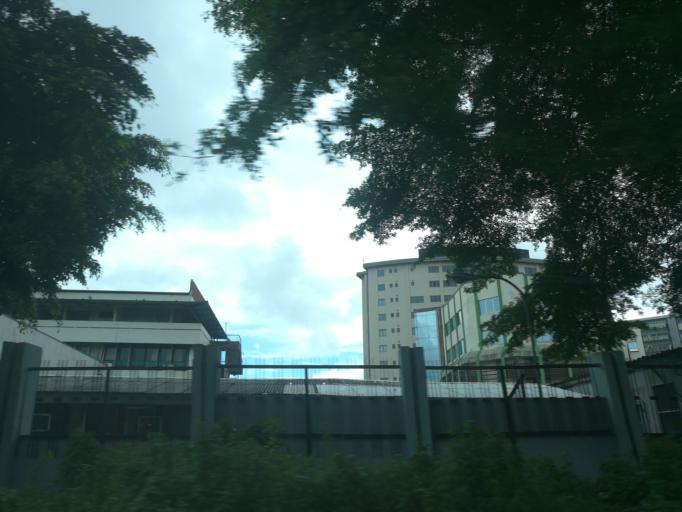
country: NG
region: Lagos
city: Ikoyi
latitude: 6.4362
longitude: 3.4151
